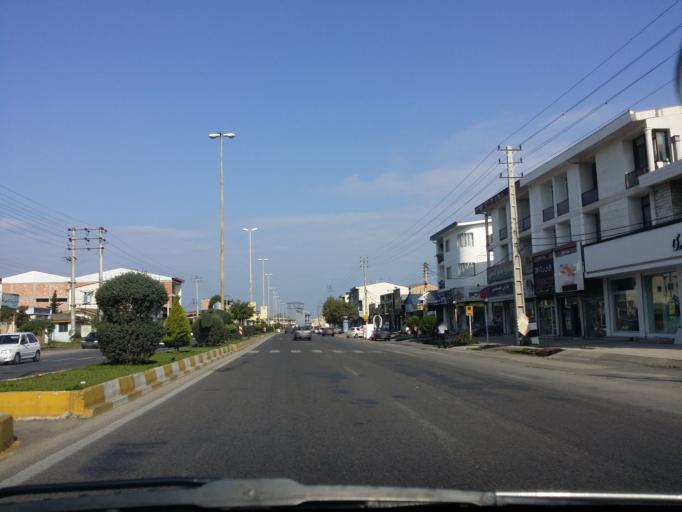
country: IR
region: Mazandaran
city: Chalus
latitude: 36.6764
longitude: 51.4045
